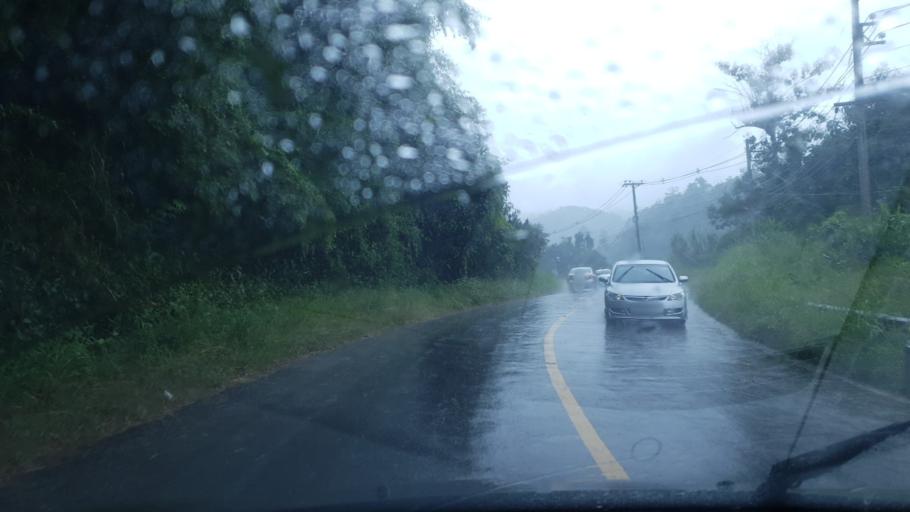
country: TH
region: Mae Hong Son
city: Khun Yuam
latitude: 18.6504
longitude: 97.9345
